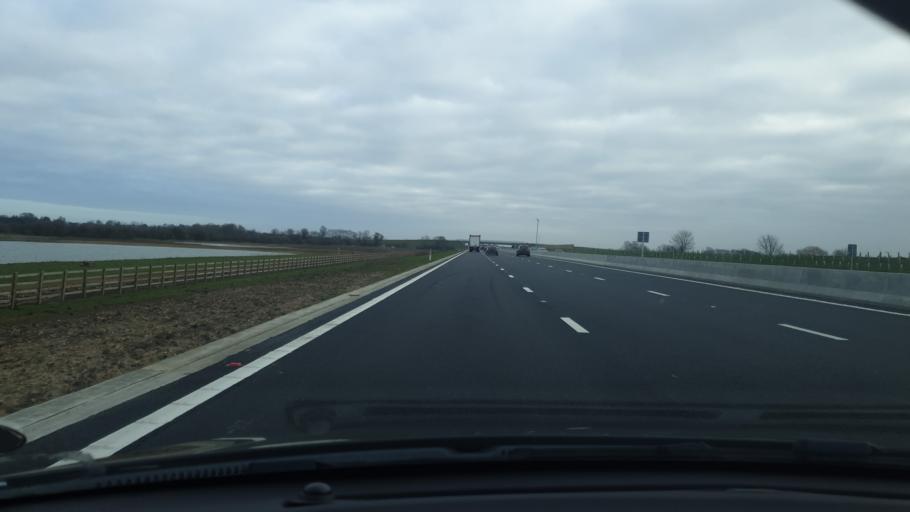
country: GB
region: England
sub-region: Cambridgeshire
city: Hemingford Grey
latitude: 52.2917
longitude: -0.0958
